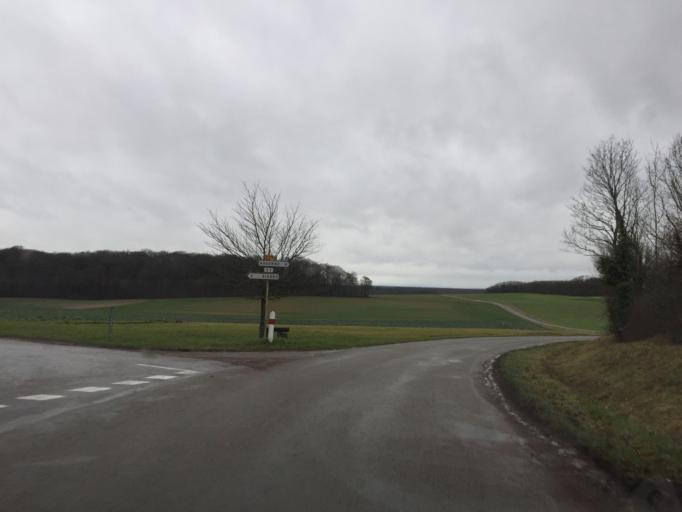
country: FR
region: Franche-Comte
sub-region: Departement du Jura
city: Dole
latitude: 47.1556
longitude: 5.4763
